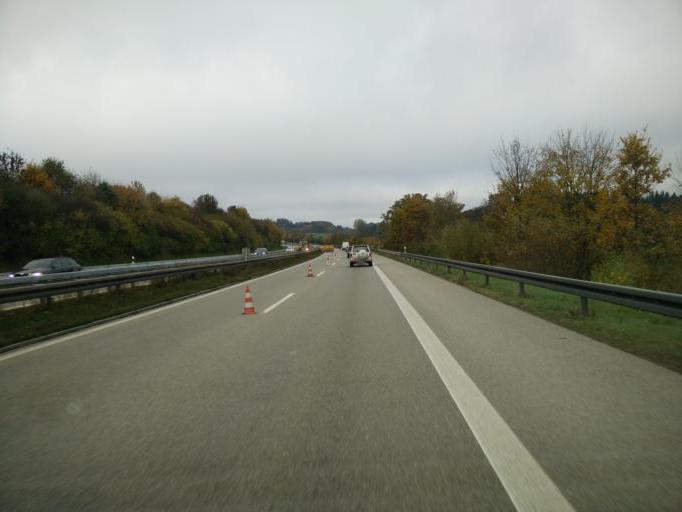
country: DE
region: Bavaria
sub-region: Swabia
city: Bad Worishofen
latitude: 48.0427
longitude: 10.5800
